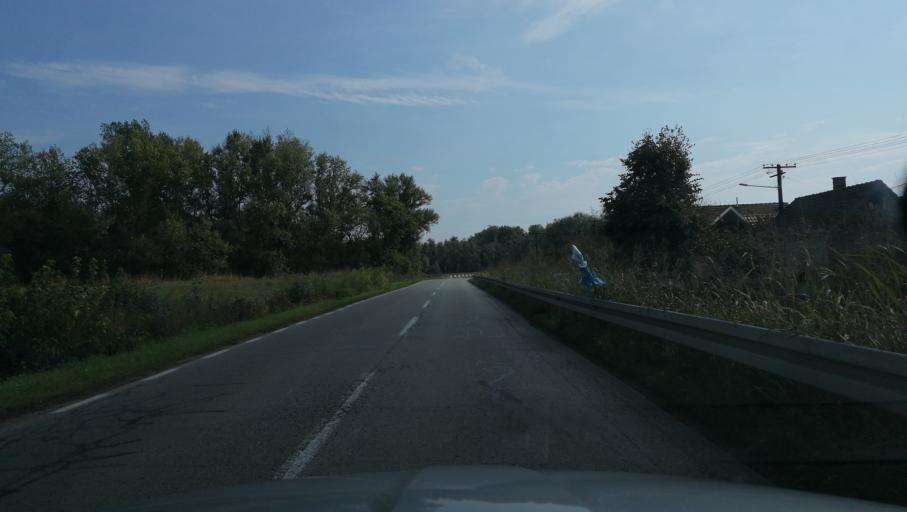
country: RS
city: Bosut
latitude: 44.9405
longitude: 19.3672
